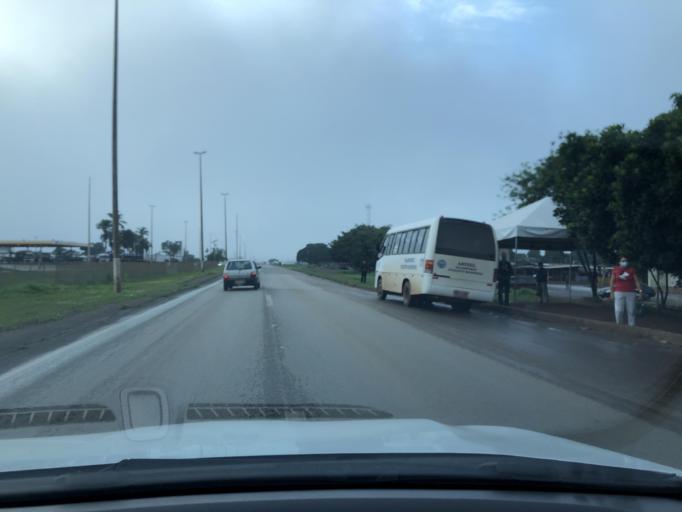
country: BR
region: Goias
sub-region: Luziania
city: Luziania
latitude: -16.1476
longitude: -47.9432
